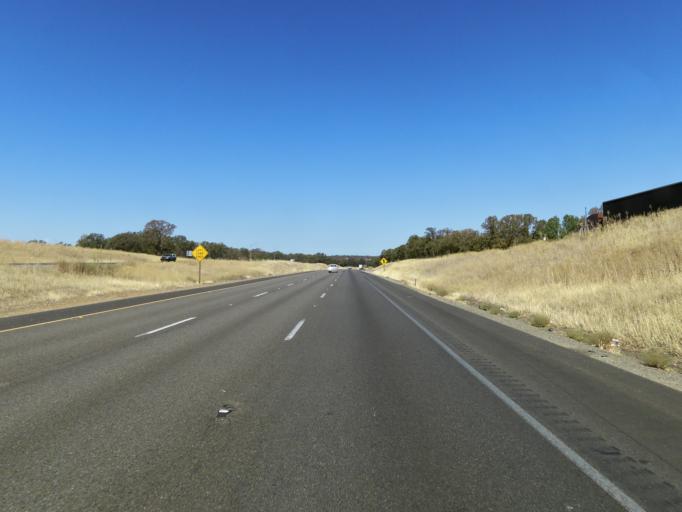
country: US
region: California
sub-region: Tehama County
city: Red Bluff
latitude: 40.2193
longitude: -122.2515
